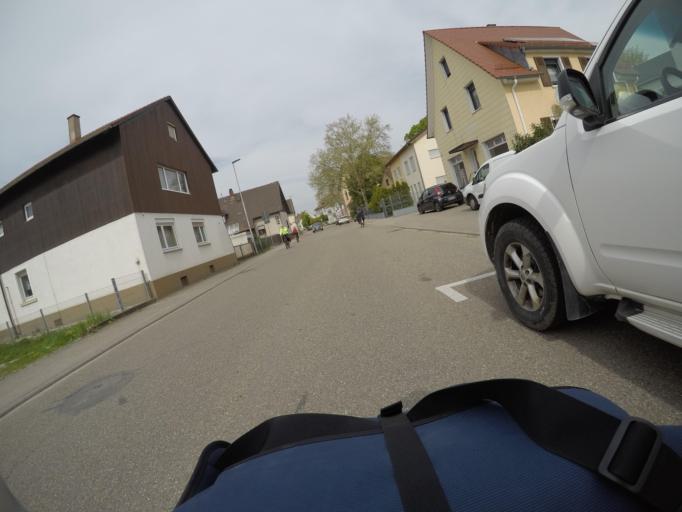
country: DE
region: Baden-Wuerttemberg
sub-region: Karlsruhe Region
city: Iffezheim
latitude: 48.8213
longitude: 8.1467
